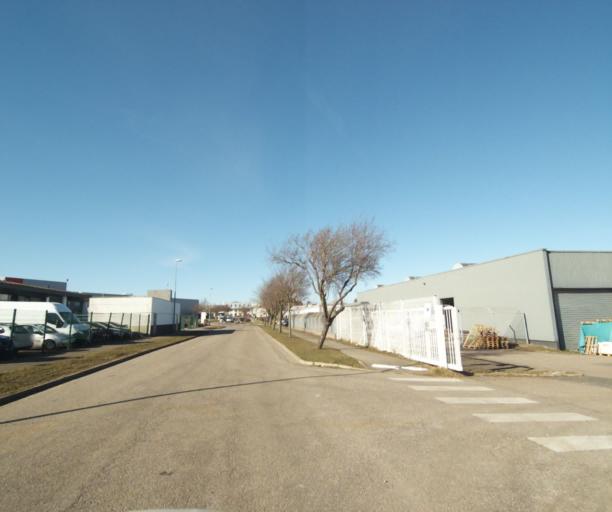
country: FR
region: Lorraine
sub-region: Departement de Meurthe-et-Moselle
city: Vandoeuvre-les-Nancy
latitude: 48.6416
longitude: 6.1880
